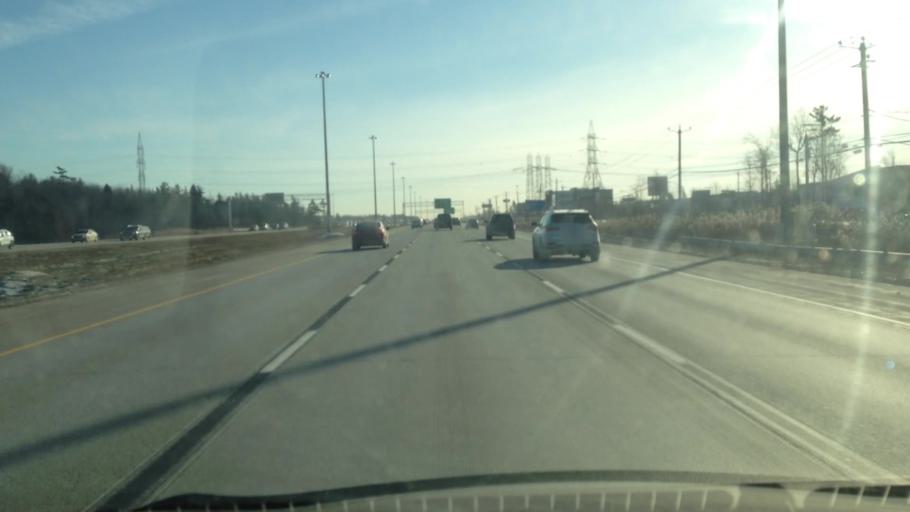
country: CA
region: Quebec
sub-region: Laurentides
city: Blainville
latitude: 45.6849
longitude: -73.9259
